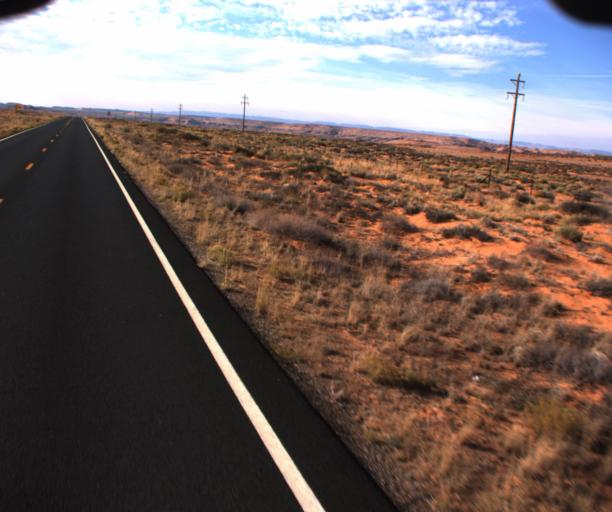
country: US
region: Arizona
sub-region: Apache County
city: Many Farms
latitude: 36.8286
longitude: -109.6440
